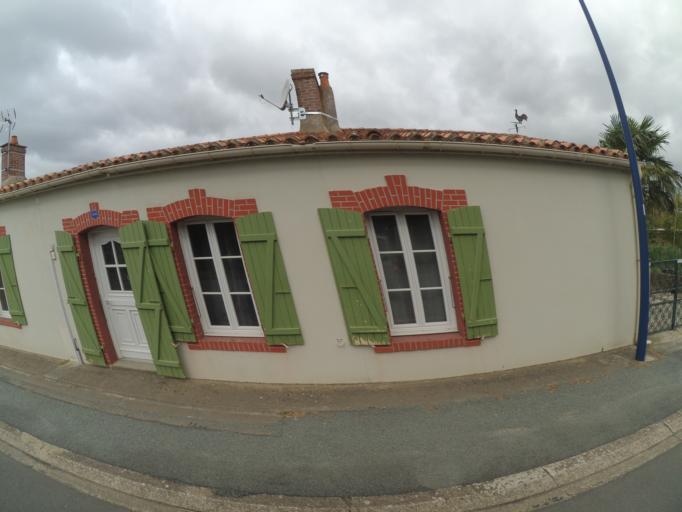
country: FR
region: Pays de la Loire
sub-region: Departement de la Vendee
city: Triaize
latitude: 46.4007
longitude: -1.2982
